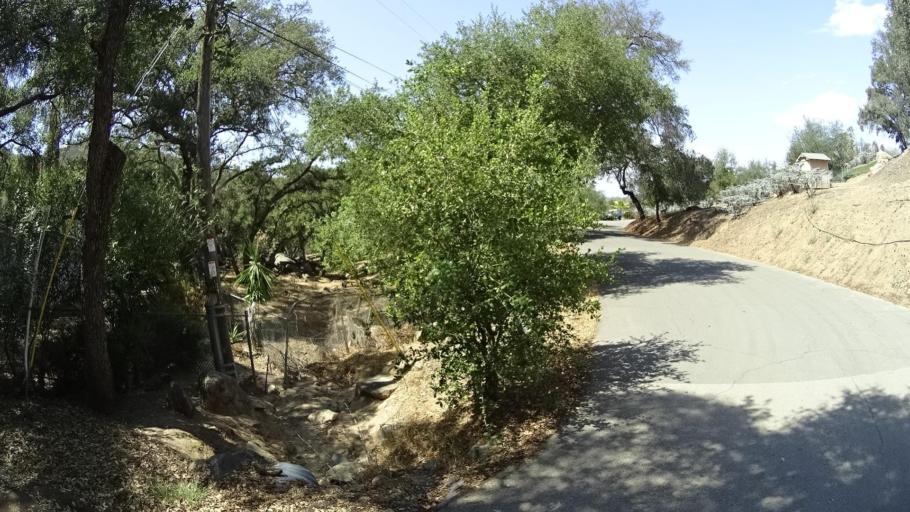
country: US
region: California
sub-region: San Diego County
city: Valley Center
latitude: 33.2019
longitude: -117.0289
